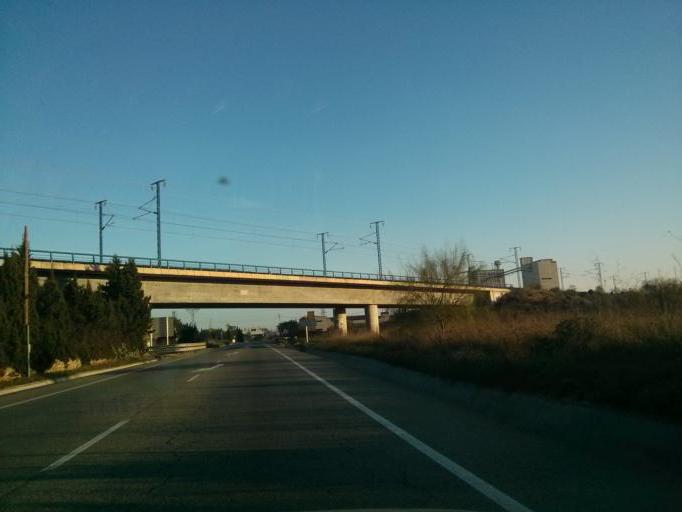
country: ES
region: Catalonia
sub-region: Provincia de Tarragona
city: El Vendrell
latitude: 41.2322
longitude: 1.5416
